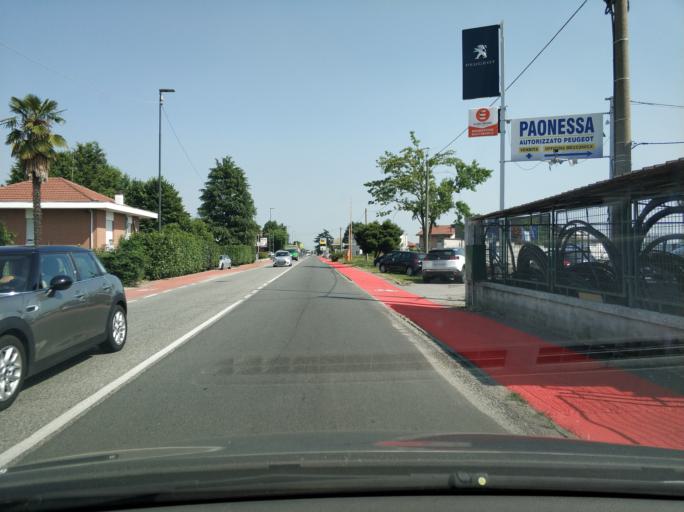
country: IT
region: Piedmont
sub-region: Provincia di Torino
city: Rivarolo Canavese
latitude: 45.3168
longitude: 7.7340
